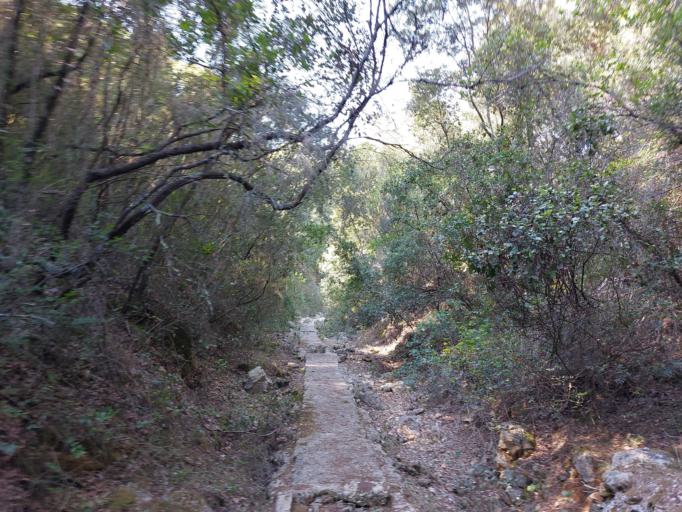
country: HR
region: Dubrovacko-Neretvanska
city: Smokvica
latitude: 42.7403
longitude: 16.8247
